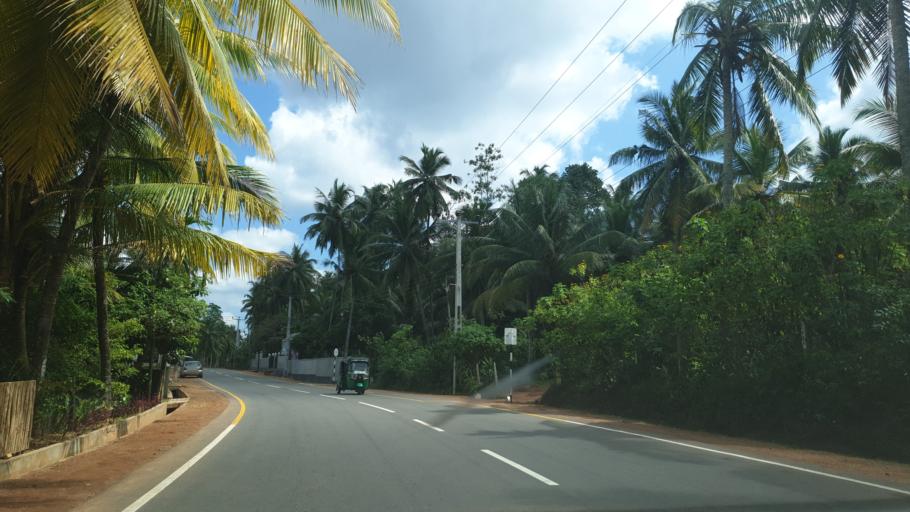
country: LK
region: Western
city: Panadura
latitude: 6.6646
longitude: 79.9529
